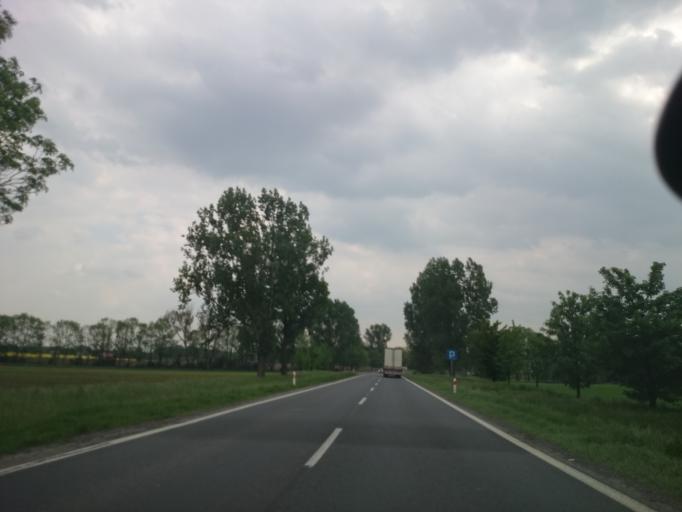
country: PL
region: Lower Silesian Voivodeship
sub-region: Powiat wroclawski
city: Kobierzyce
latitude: 50.9574
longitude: 16.9162
